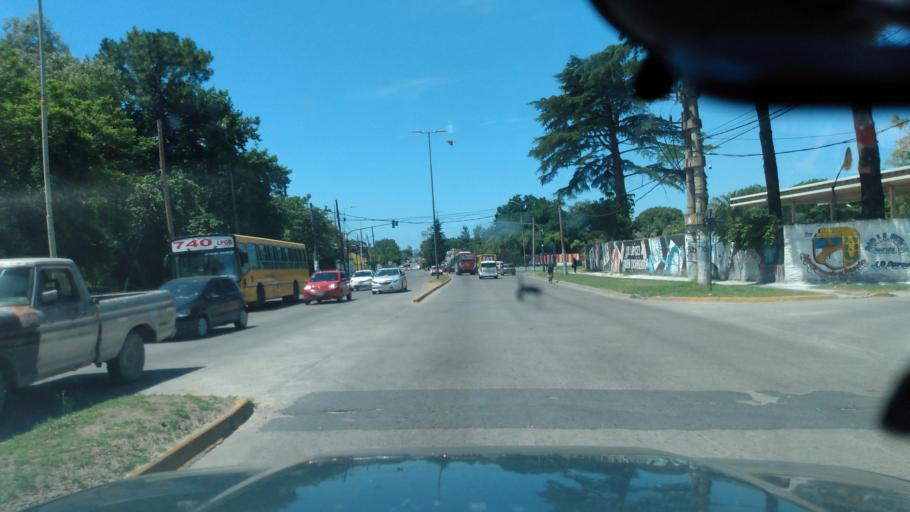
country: AR
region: Buenos Aires
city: Hurlingham
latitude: -34.5578
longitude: -58.7287
